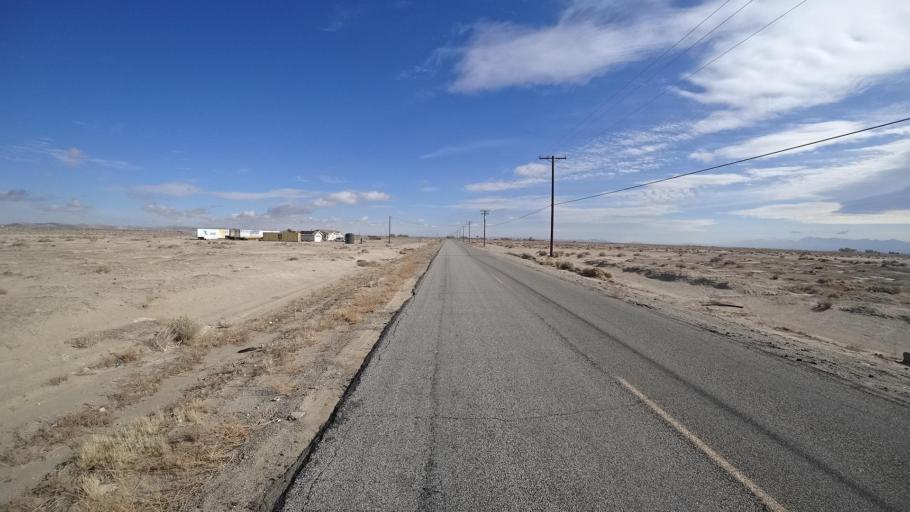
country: US
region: California
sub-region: Kern County
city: Rosamond
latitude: 34.8201
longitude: -118.2078
